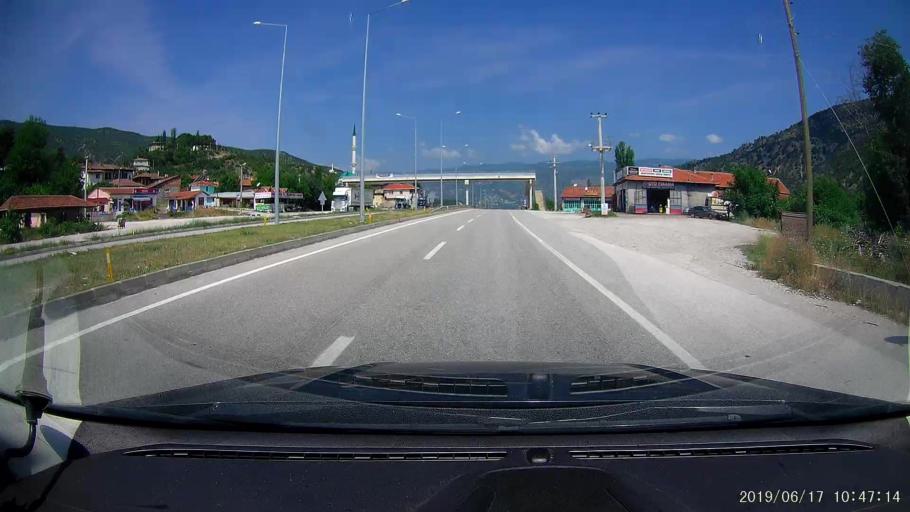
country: TR
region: Corum
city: Hacihamza
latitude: 41.0753
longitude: 34.4521
